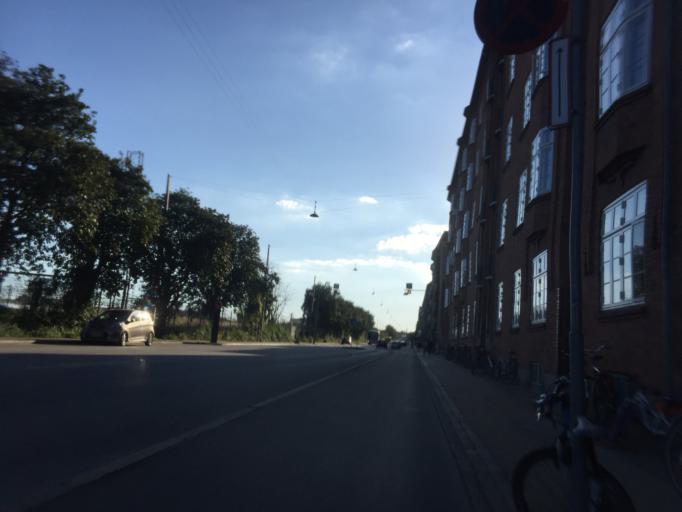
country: DK
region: Capital Region
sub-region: Kobenhavn
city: Copenhagen
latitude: 55.6643
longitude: 12.5506
